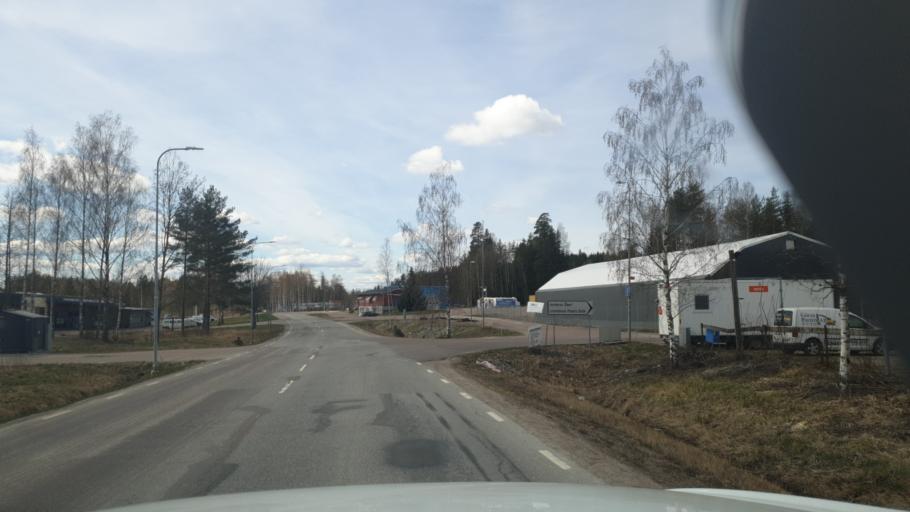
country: SE
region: Vaermland
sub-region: Arvika Kommun
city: Arvika
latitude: 59.6637
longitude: 12.6325
